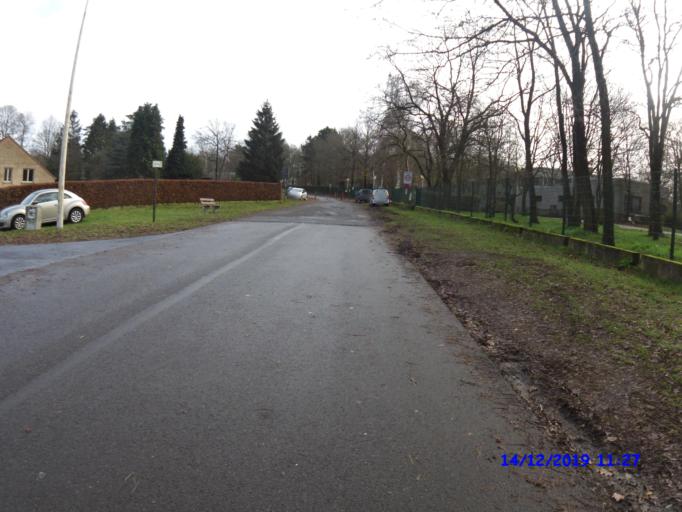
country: BE
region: Flanders
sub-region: Provincie Vlaams-Brabant
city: Beersel
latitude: 50.7281
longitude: 4.3184
